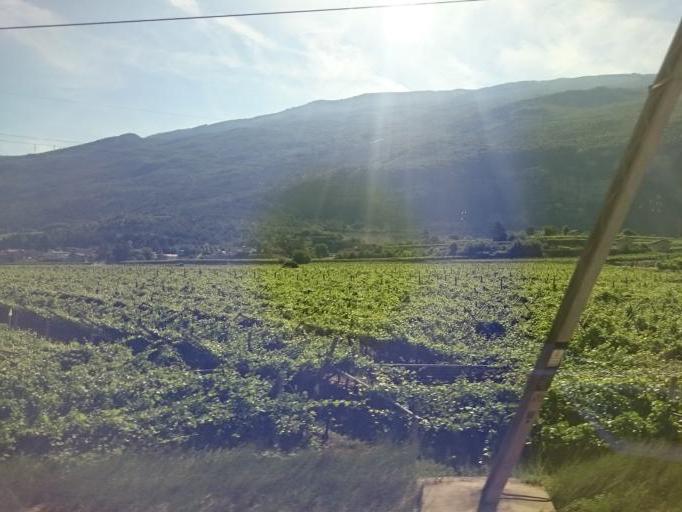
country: IT
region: Trentino-Alto Adige
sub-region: Provincia di Trento
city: Marco
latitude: 45.8328
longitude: 11.0031
